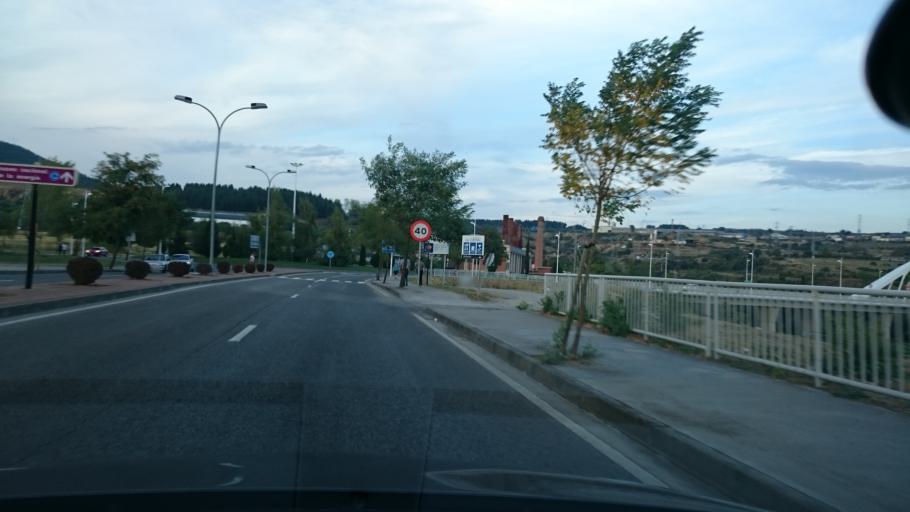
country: ES
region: Castille and Leon
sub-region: Provincia de Leon
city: Ponferrada
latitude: 42.5566
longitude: -6.5932
